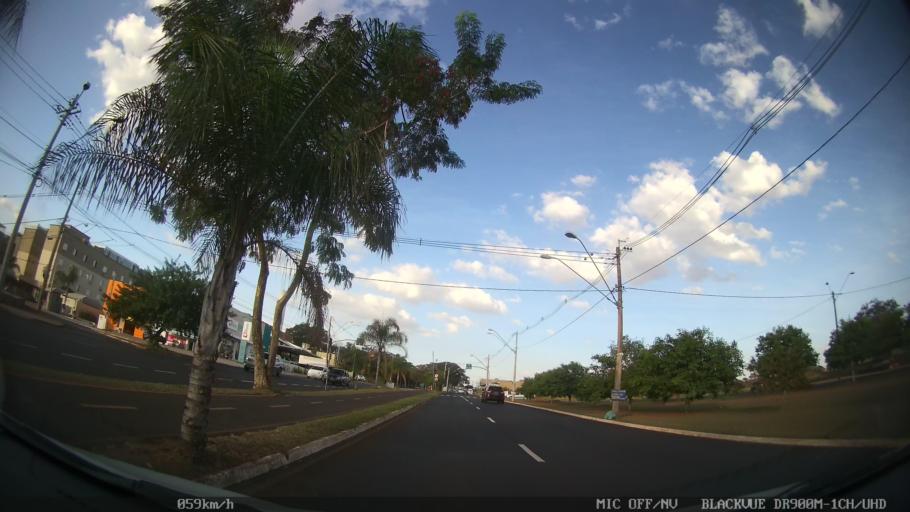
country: BR
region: Sao Paulo
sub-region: Ribeirao Preto
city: Ribeirao Preto
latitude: -21.1936
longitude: -47.7498
